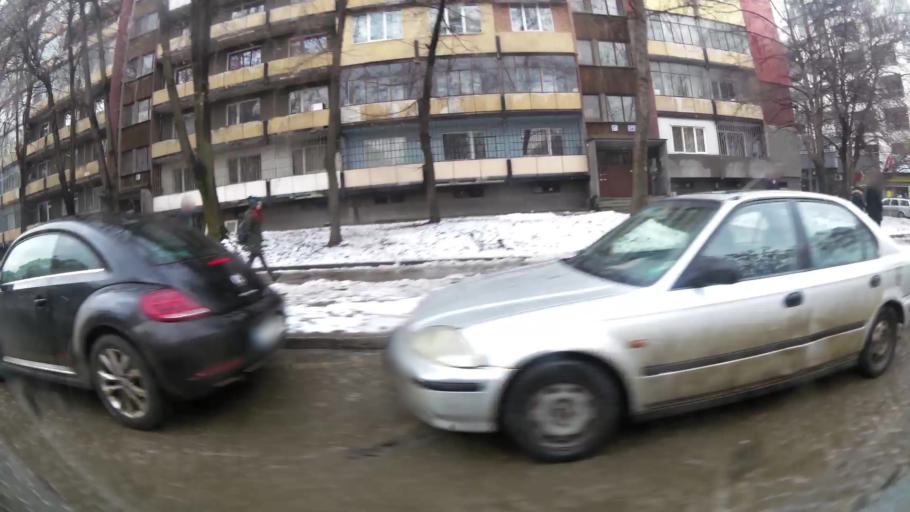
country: BG
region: Sofia-Capital
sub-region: Stolichna Obshtina
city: Sofia
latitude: 42.6708
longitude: 23.2957
